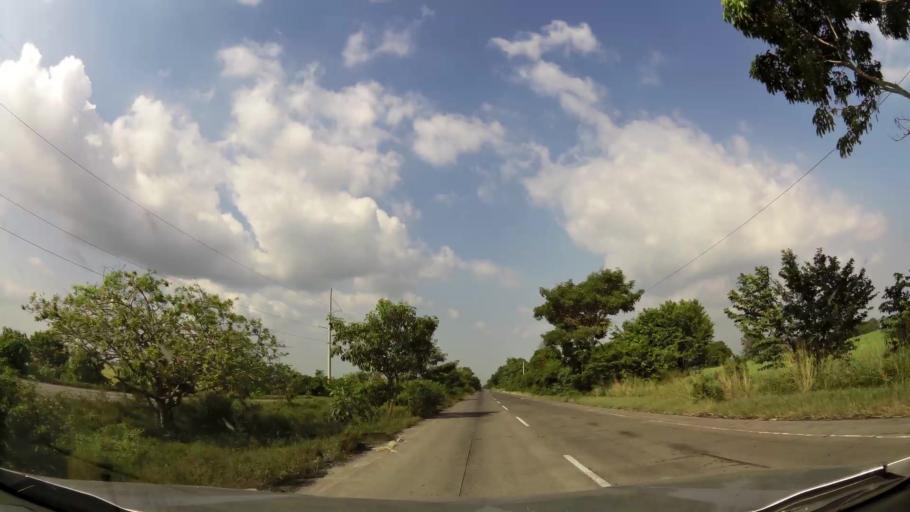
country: GT
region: Escuintla
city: Puerto San Jose
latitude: 14.0237
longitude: -90.7824
